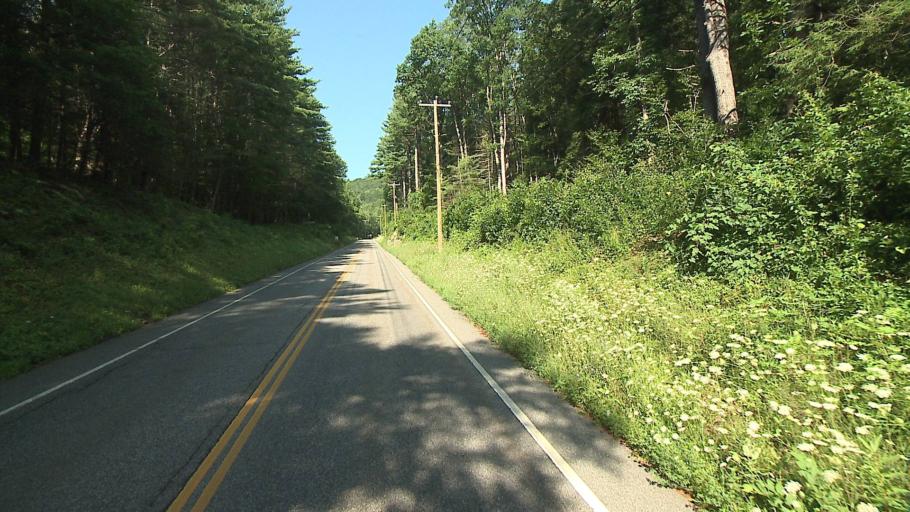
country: US
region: Connecticut
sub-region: Litchfield County
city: Kent
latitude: 41.8212
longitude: -73.3789
